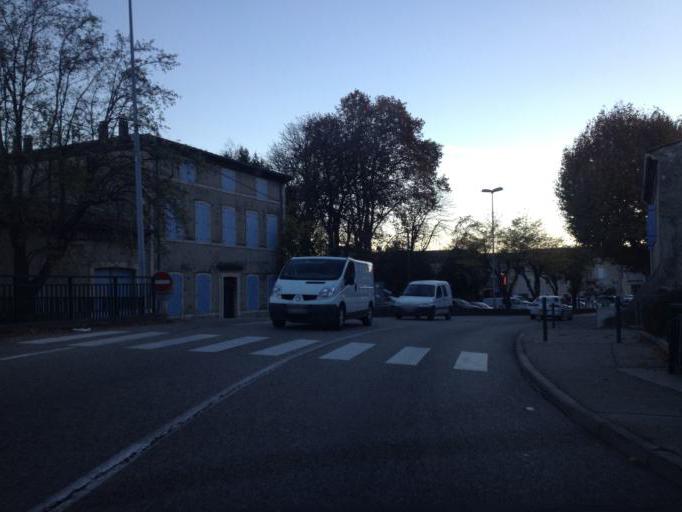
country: FR
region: Rhone-Alpes
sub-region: Departement de l'Ardeche
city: Rochemaure
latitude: 44.5889
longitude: 4.7054
